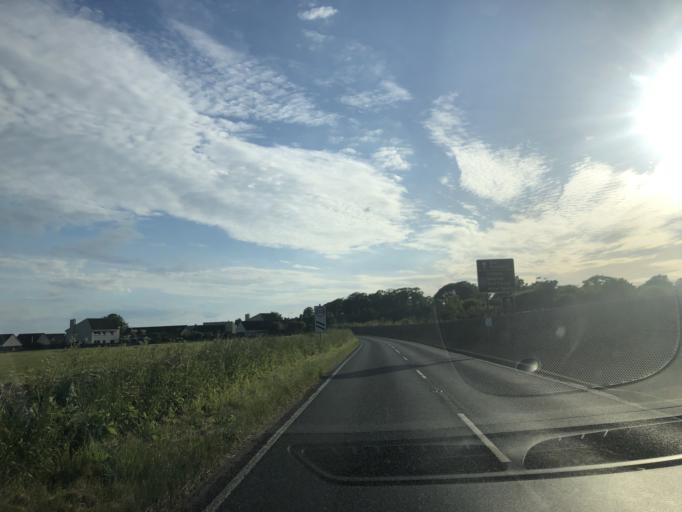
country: GB
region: Scotland
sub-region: Fife
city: Saint Monance
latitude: 56.1926
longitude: -2.8109
